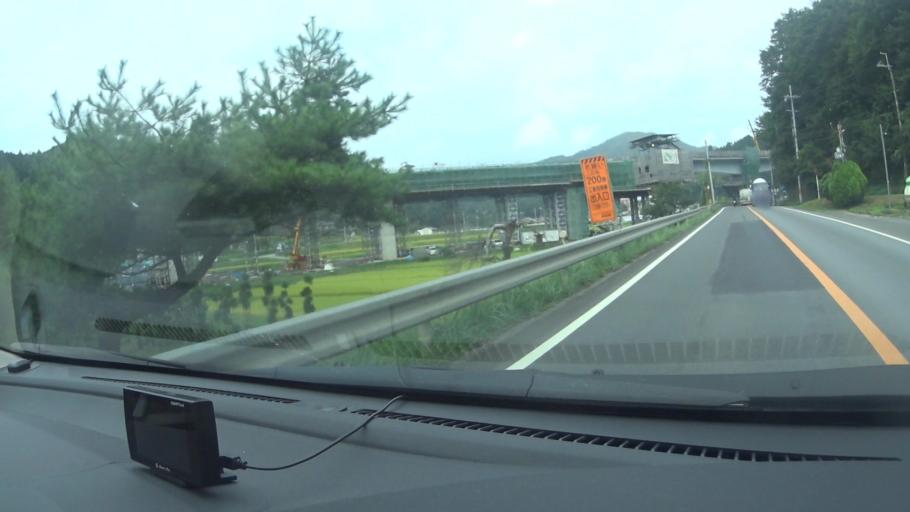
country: JP
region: Kyoto
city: Ayabe
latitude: 35.2179
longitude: 135.3436
